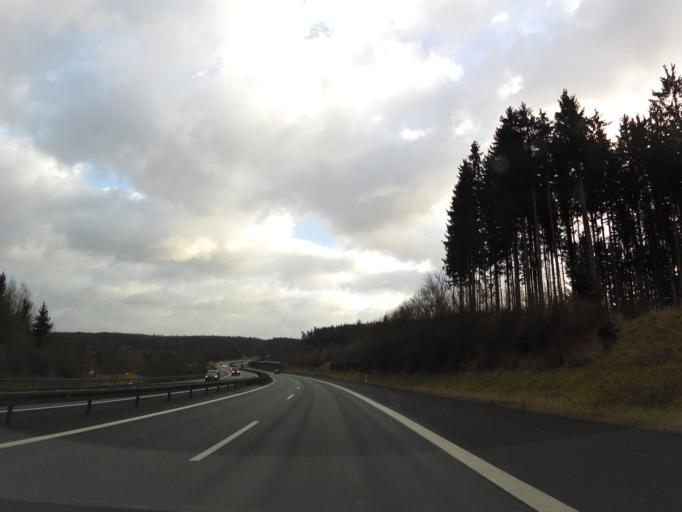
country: DE
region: Bavaria
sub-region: Upper Franconia
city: Thierstein
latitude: 50.1399
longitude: 12.0843
